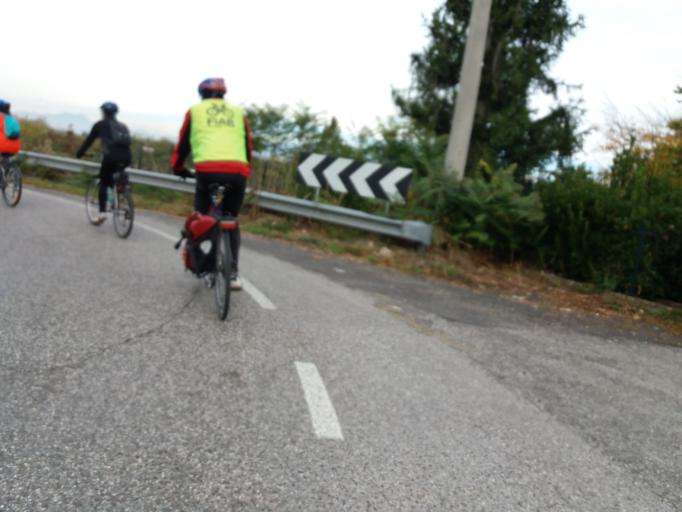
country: IT
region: Veneto
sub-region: Provincia di Verona
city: Parona
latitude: 45.4640
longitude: 10.9312
